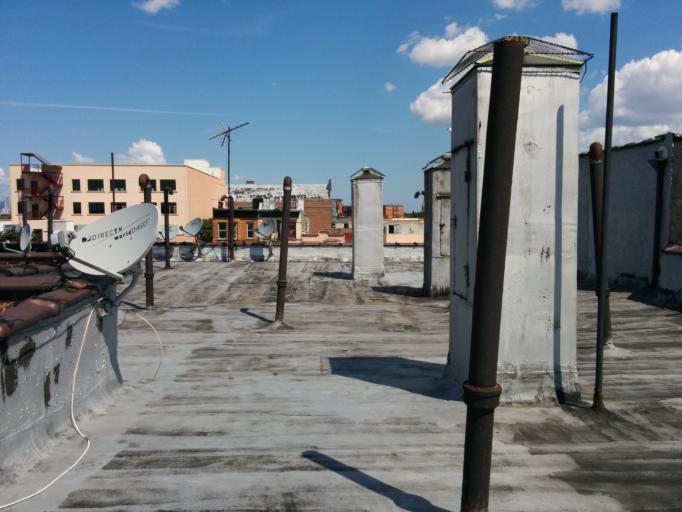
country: US
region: New York
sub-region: Kings County
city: East New York
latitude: 40.6881
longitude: -73.9227
